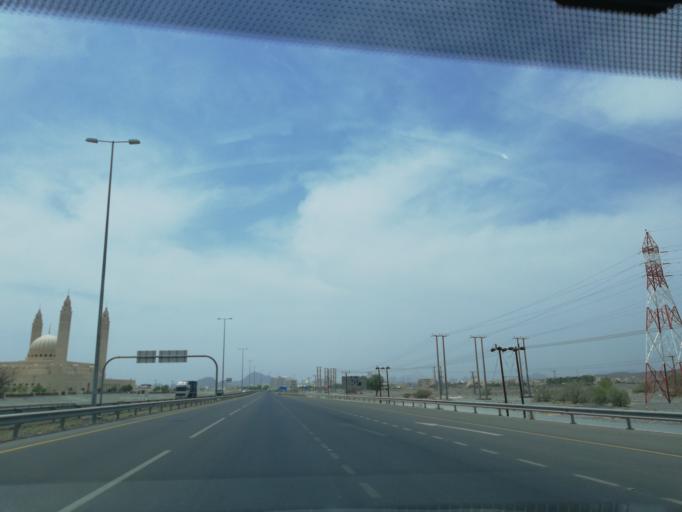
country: OM
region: Muhafazat ad Dakhiliyah
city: Nizwa
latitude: 22.8578
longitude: 57.5336
